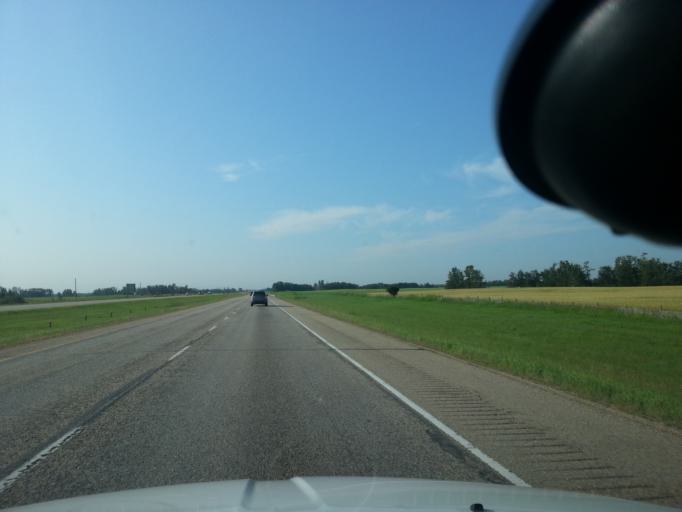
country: CA
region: Alberta
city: Ponoka
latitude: 52.8900
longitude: -113.6442
